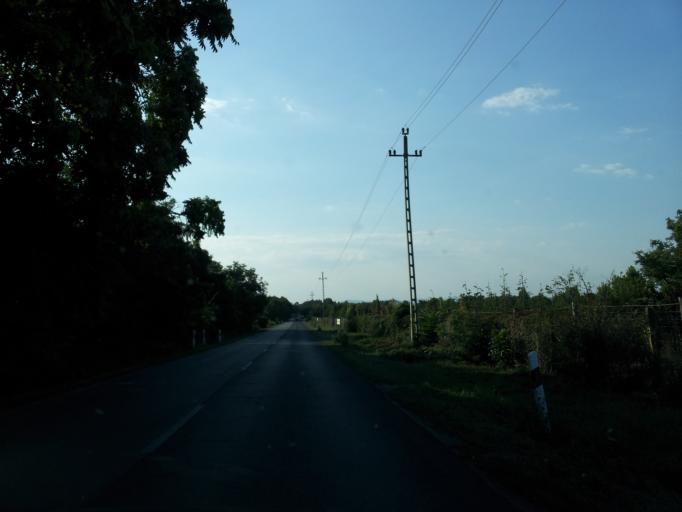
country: HU
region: Pest
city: Dunabogdany
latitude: 47.7659
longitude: 19.0645
